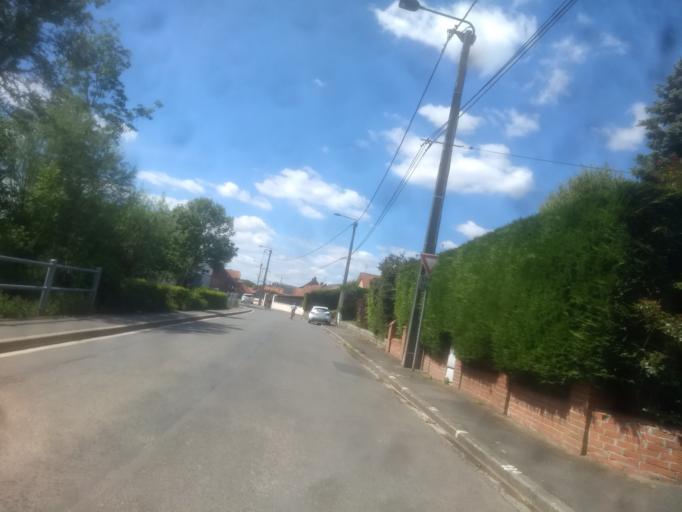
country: FR
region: Nord-Pas-de-Calais
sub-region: Departement du Pas-de-Calais
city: Riviere
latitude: 50.2464
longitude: 2.7213
